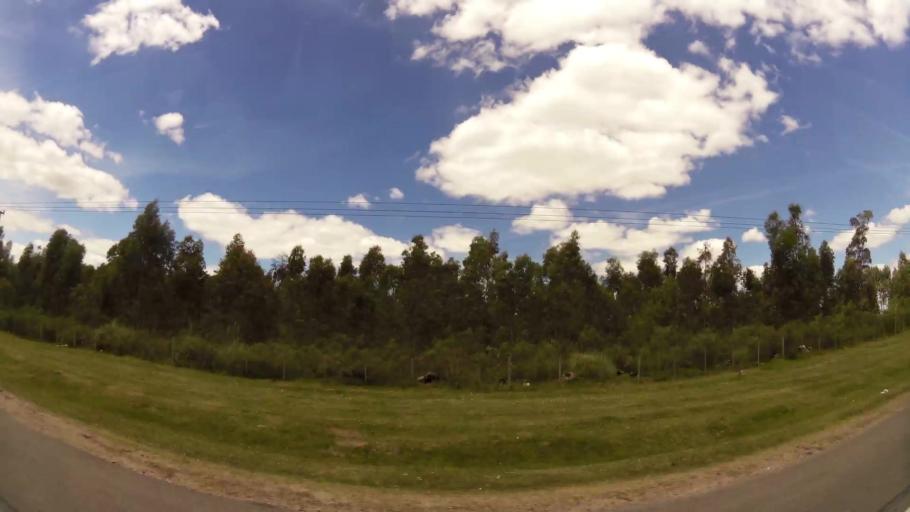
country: UY
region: Canelones
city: Pando
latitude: -34.8048
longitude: -55.9564
